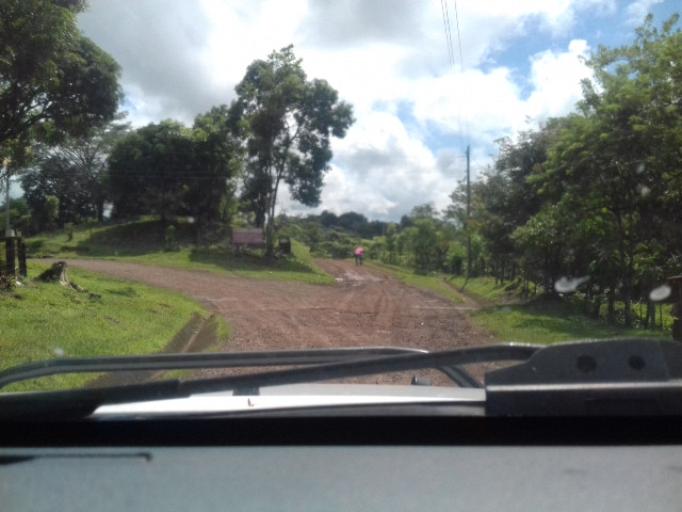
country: NI
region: Matagalpa
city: Rio Blanco
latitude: 12.9763
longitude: -85.1846
